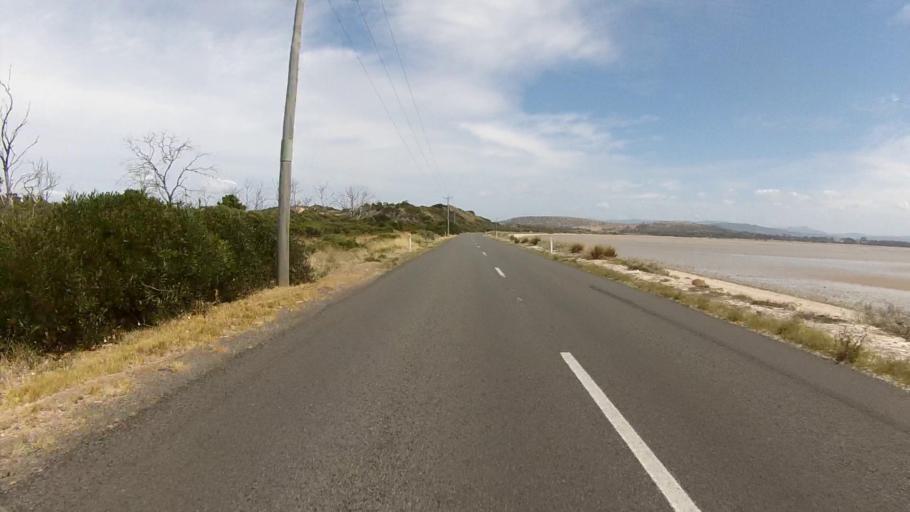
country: AU
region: Tasmania
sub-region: Clarence
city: Sandford
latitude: -43.0301
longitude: 147.4626
